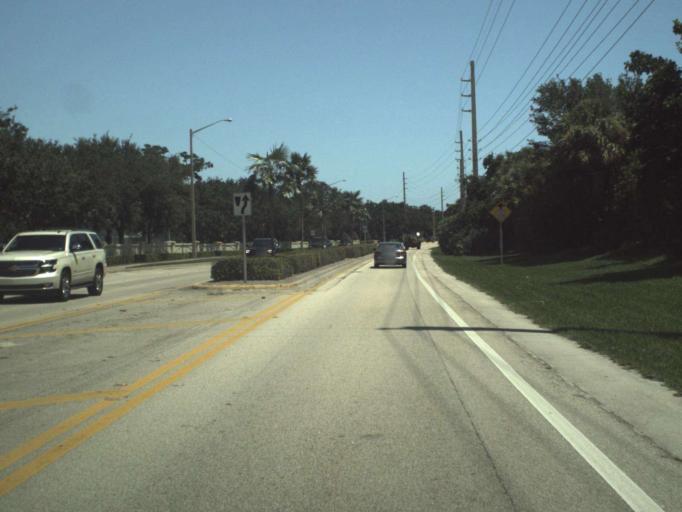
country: US
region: Florida
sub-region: Indian River County
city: Vero Beach
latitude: 27.6418
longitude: -80.3601
